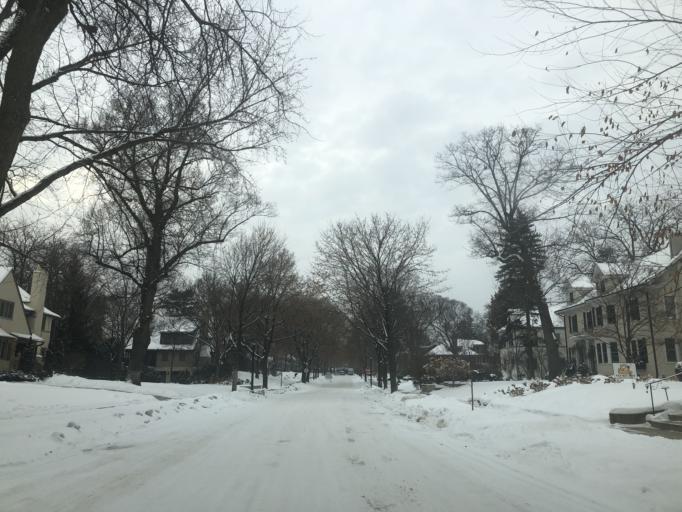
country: US
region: Minnesota
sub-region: Hennepin County
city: Richfield
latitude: 44.9237
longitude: -93.2950
